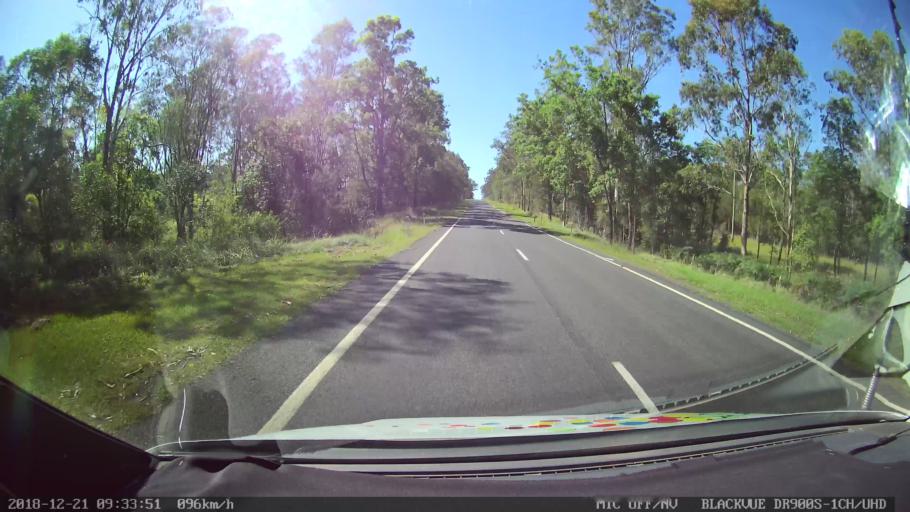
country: AU
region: New South Wales
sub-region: Clarence Valley
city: Grafton
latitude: -29.4903
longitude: 152.9775
